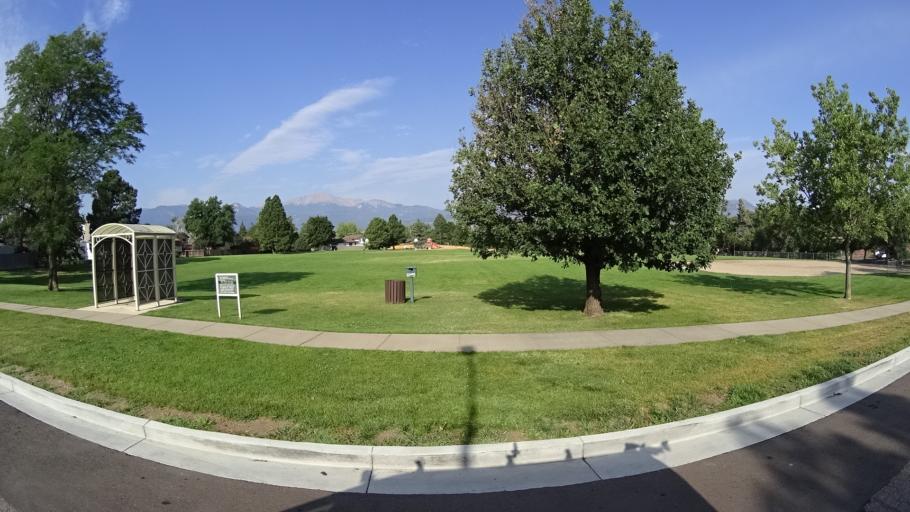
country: US
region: Colorado
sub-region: El Paso County
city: Colorado Springs
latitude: 38.8889
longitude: -104.8039
